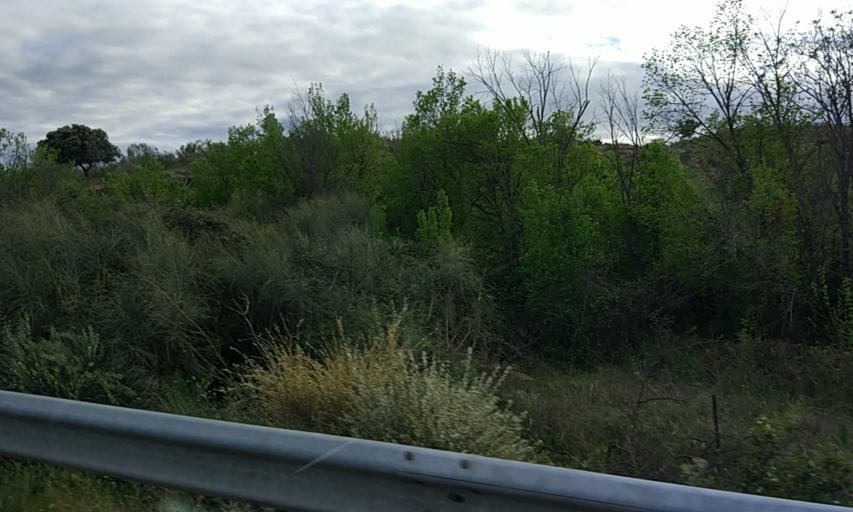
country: ES
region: Extremadura
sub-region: Provincia de Caceres
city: Coria
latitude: 39.9550
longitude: -6.5106
